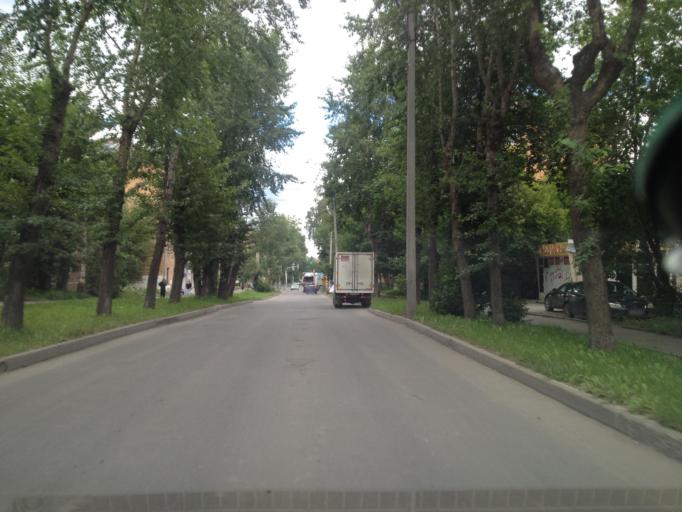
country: RU
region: Sverdlovsk
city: Shuvakish
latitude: 56.8694
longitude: 60.5275
